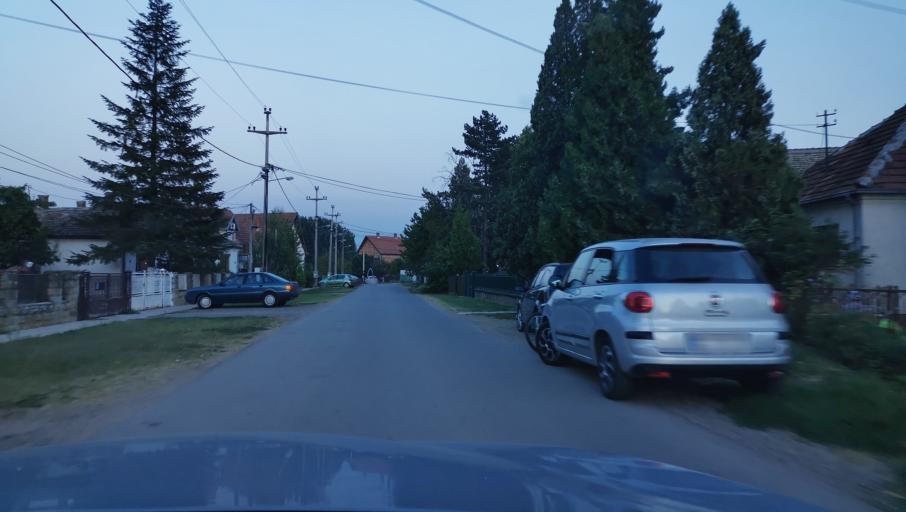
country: RS
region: Central Serbia
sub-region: Belgrade
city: Obrenovac
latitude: 44.6814
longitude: 20.2199
